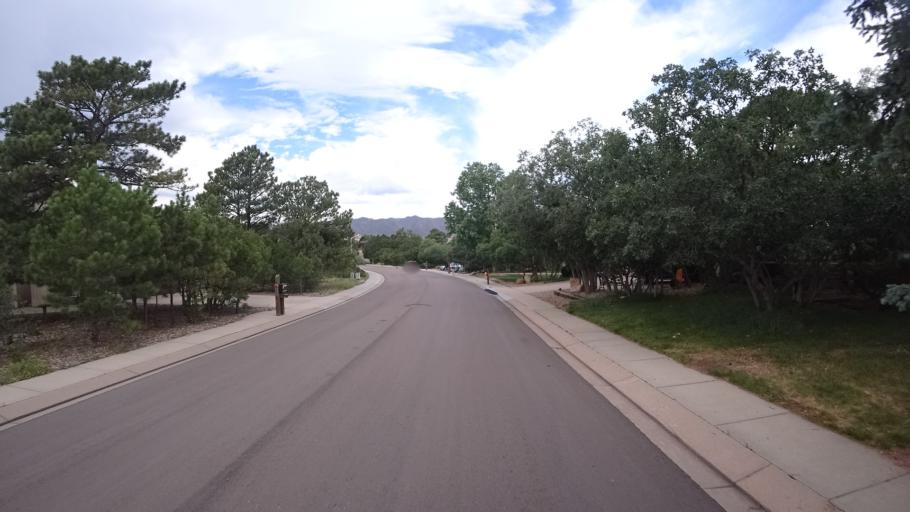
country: US
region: Colorado
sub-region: El Paso County
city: Colorado Springs
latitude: 38.9059
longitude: -104.8453
